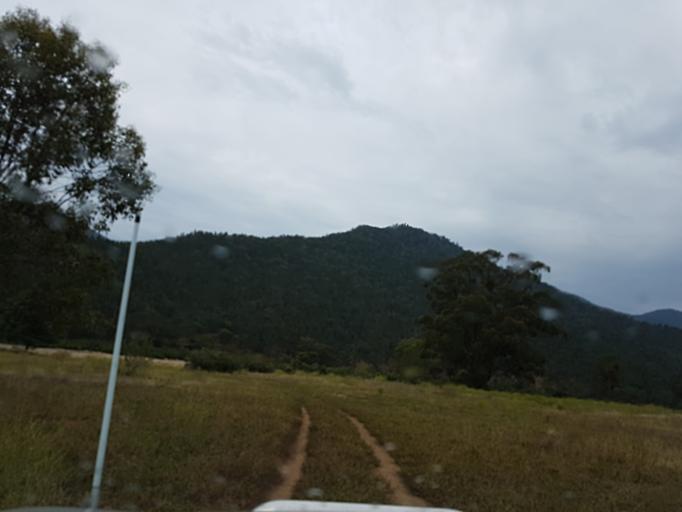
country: AU
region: New South Wales
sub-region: Snowy River
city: Jindabyne
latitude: -36.9528
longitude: 148.4052
